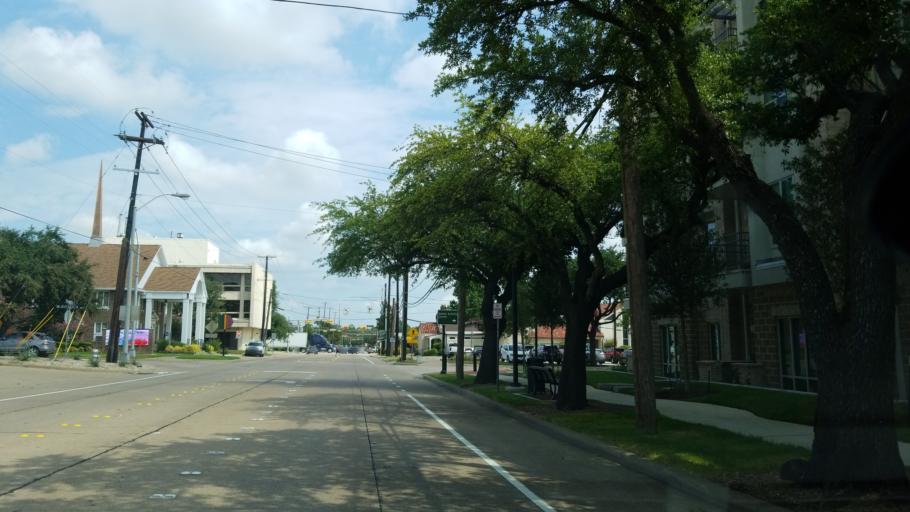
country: US
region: Texas
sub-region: Dallas County
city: Garland
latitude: 32.9113
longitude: -96.6402
